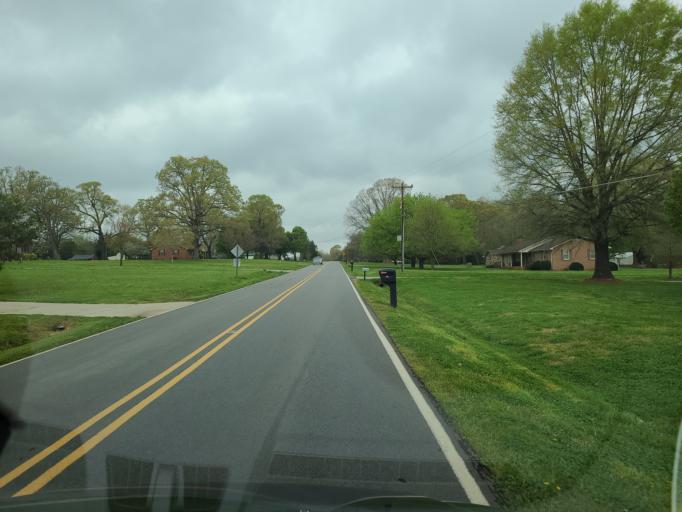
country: US
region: North Carolina
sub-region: Lincoln County
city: Lincolnton
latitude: 35.4579
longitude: -81.3149
